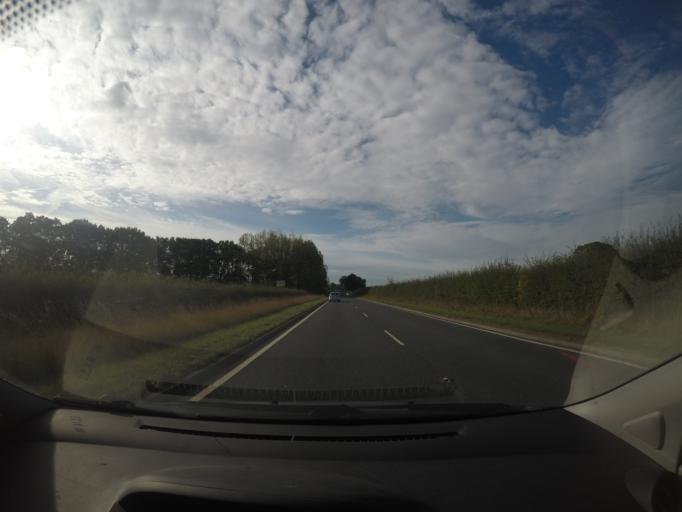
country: GB
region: England
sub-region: City of York
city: Deighton
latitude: 53.8676
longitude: -1.0499
